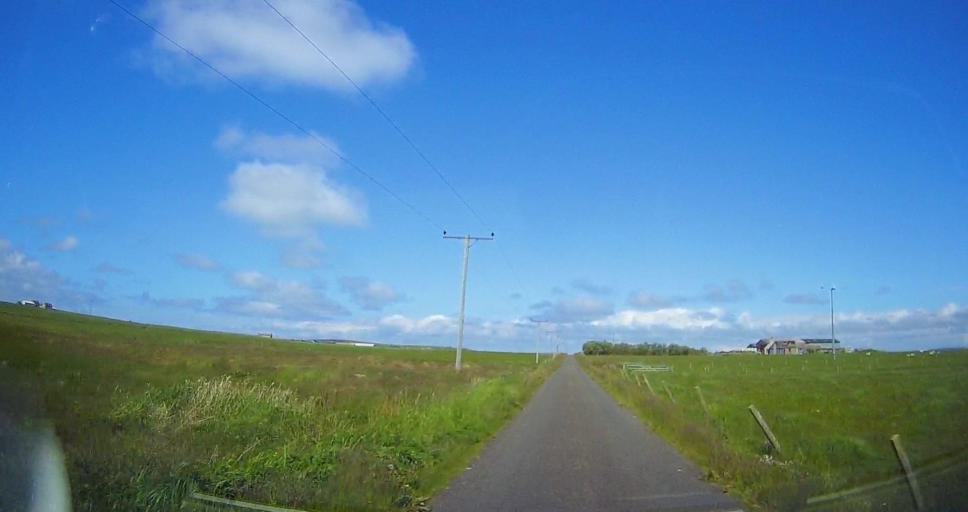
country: GB
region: Scotland
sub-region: Orkney Islands
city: Kirkwall
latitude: 58.8278
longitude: -2.8957
